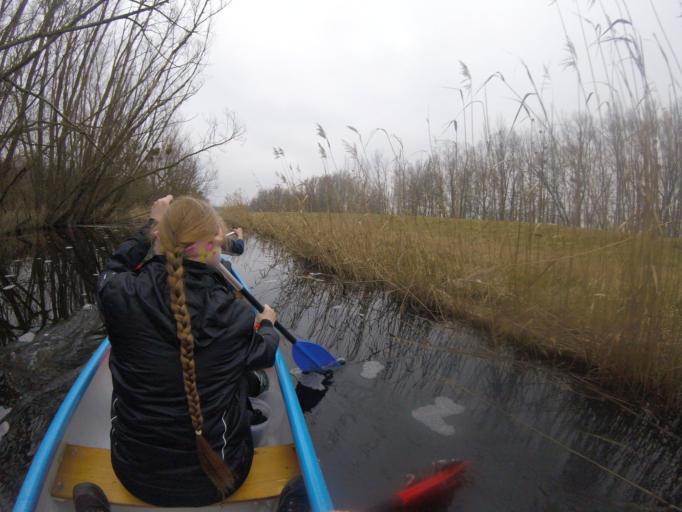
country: HU
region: Zala
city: Keszthely
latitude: 46.7342
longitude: 17.2229
